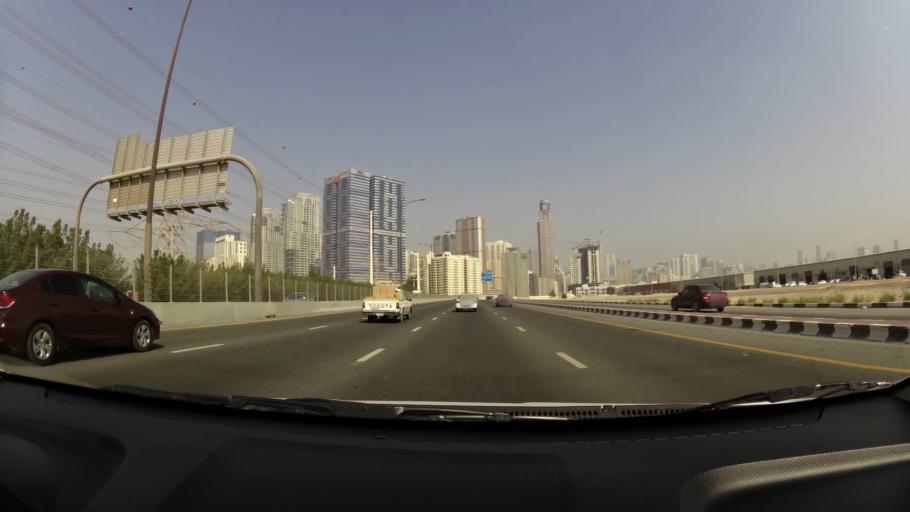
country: AE
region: Ash Shariqah
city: Sharjah
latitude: 25.3015
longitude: 55.3897
